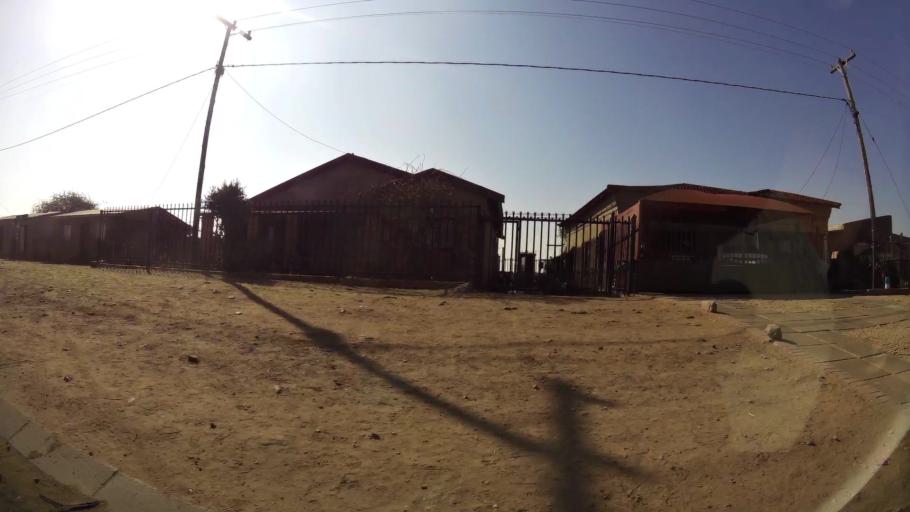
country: ZA
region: Orange Free State
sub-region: Mangaung Metropolitan Municipality
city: Bloemfontein
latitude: -29.1969
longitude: 26.2478
